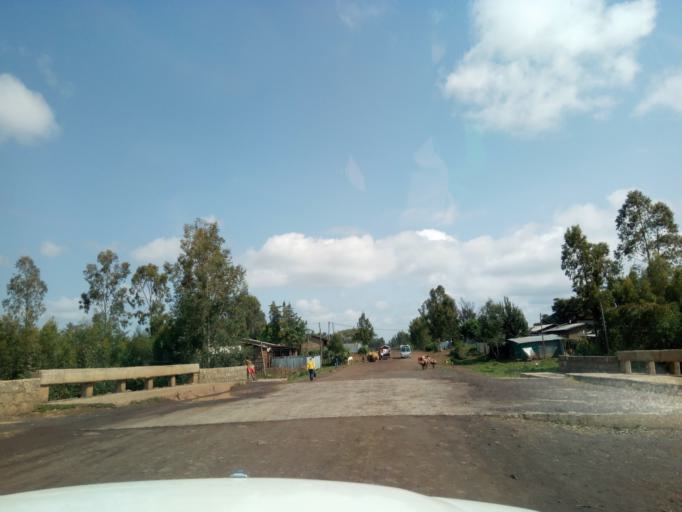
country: ET
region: Oromiya
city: Waliso
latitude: 8.5453
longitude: 37.9638
